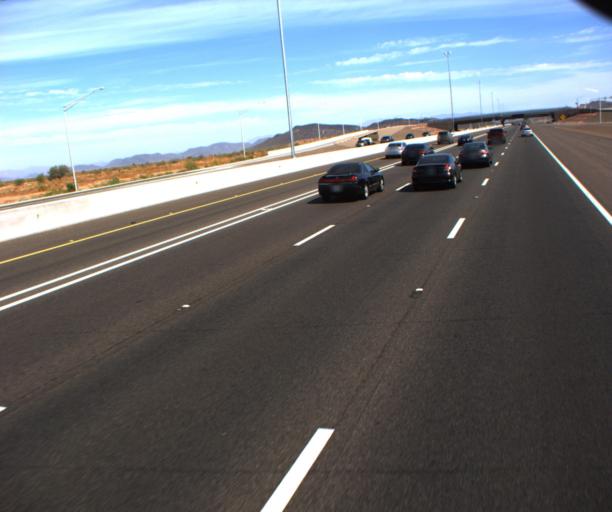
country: US
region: Arizona
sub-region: Maricopa County
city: Anthem
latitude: 33.7788
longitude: -112.1311
